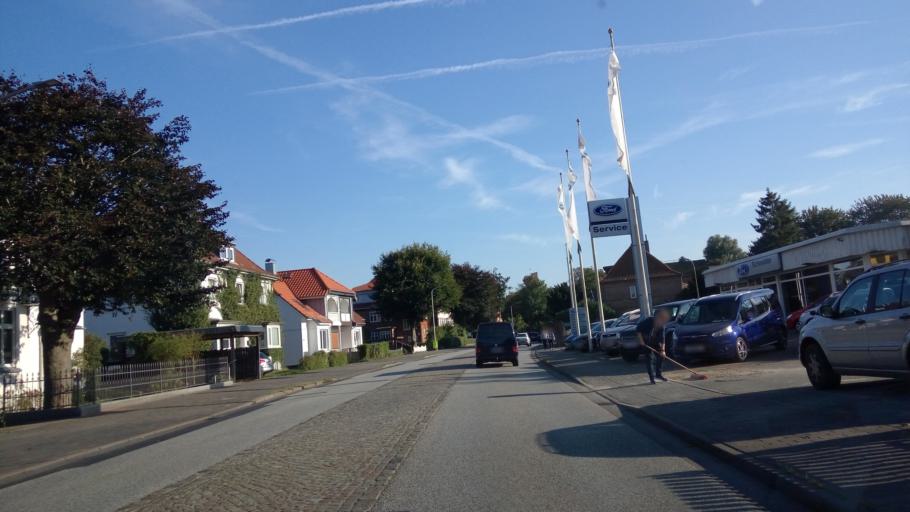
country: DE
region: Schleswig-Holstein
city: Eckernforde
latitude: 54.4628
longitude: 9.8396
